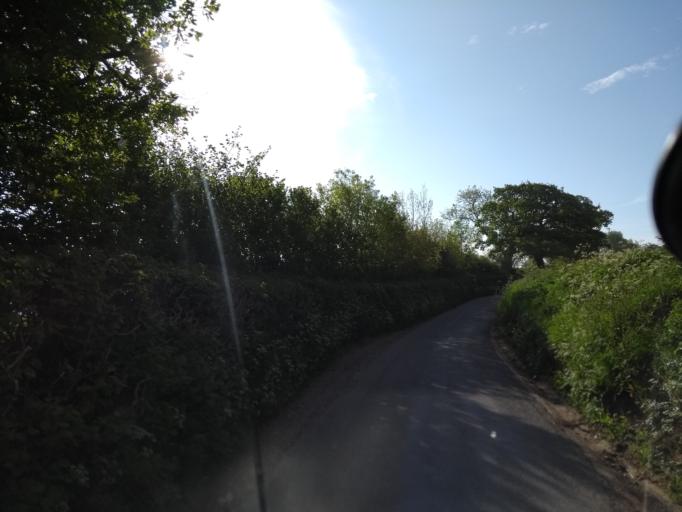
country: GB
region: England
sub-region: Devon
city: Axminster
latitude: 50.7977
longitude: -2.9305
